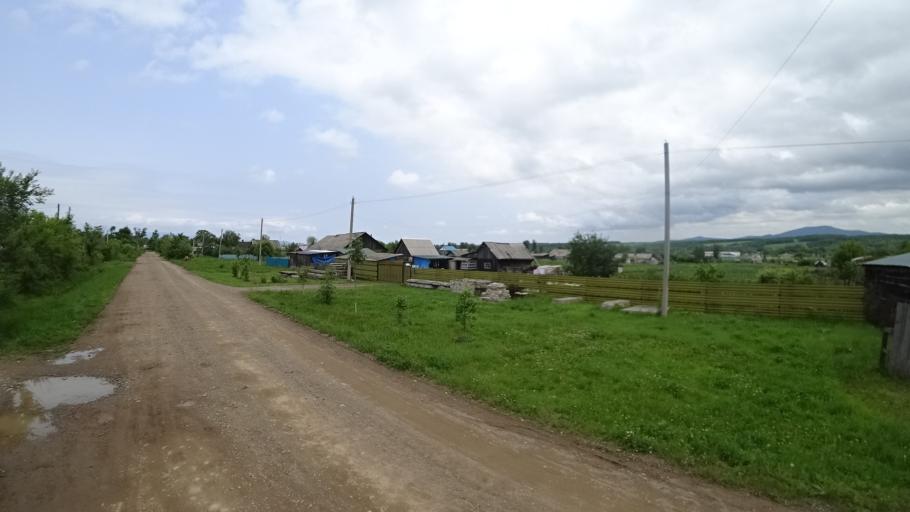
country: RU
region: Primorskiy
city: Novosysoyevka
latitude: 44.2339
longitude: 133.3649
